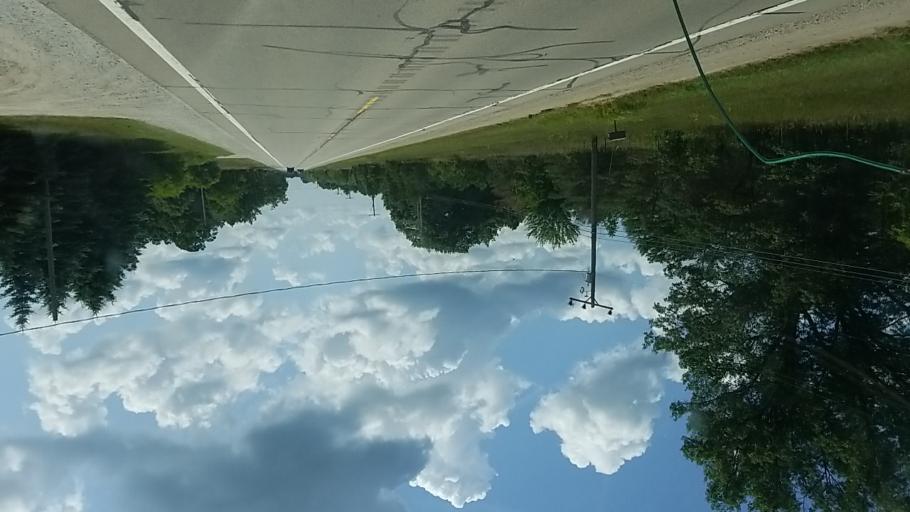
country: US
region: Michigan
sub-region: Muskegon County
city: Wolf Lake
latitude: 43.2353
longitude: -86.0448
